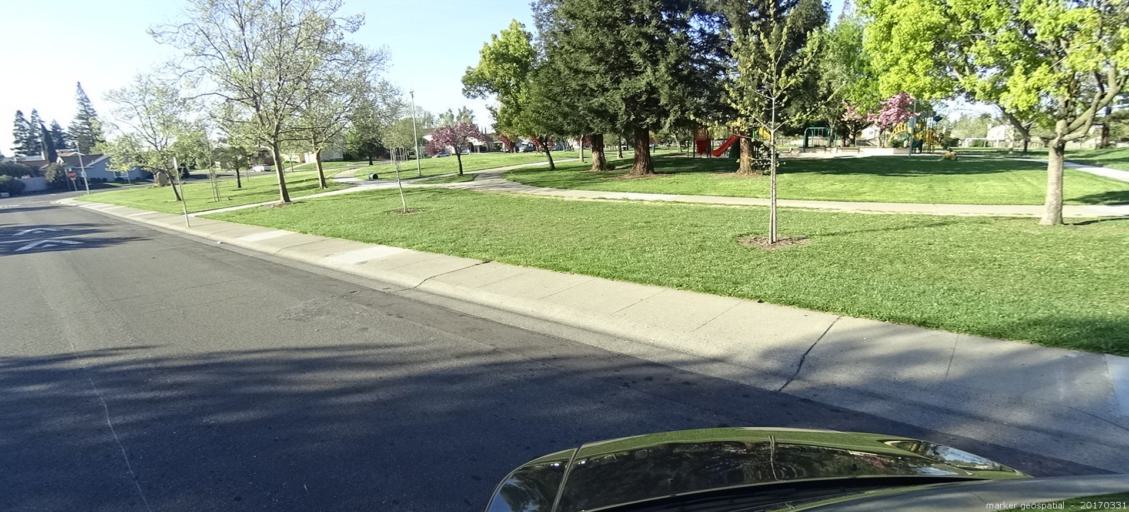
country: US
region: California
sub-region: Sacramento County
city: Parkway
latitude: 38.4671
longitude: -121.4523
